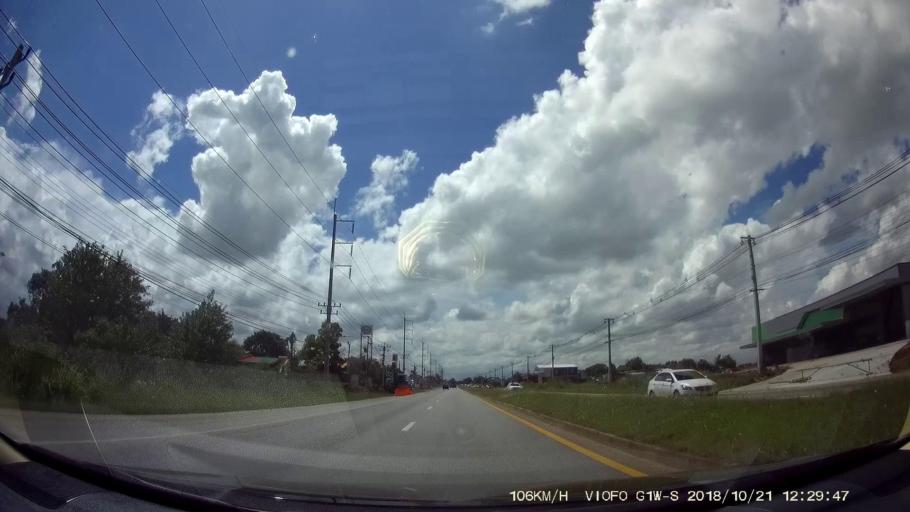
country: TH
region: Nakhon Ratchasima
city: Dan Khun Thot
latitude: 15.1781
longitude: 101.7456
